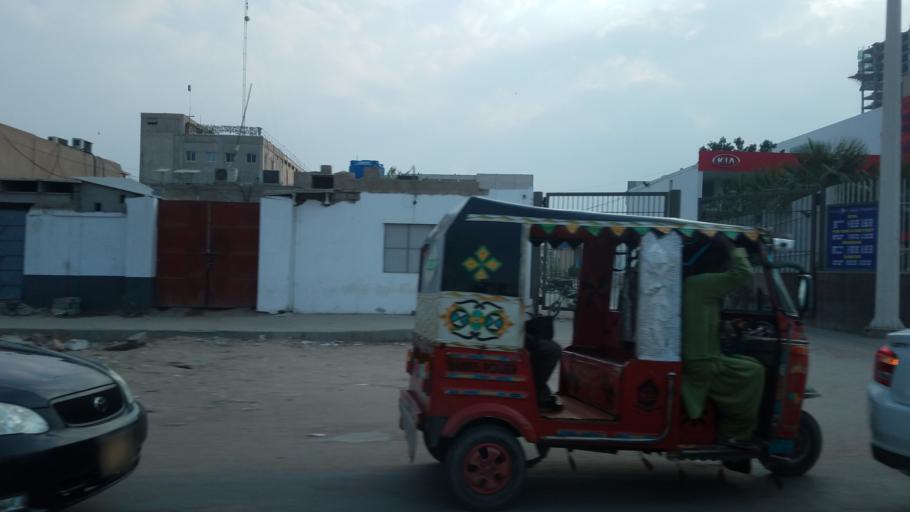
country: PK
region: Sindh
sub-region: Karachi District
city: Karachi
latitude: 24.9336
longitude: 67.0857
